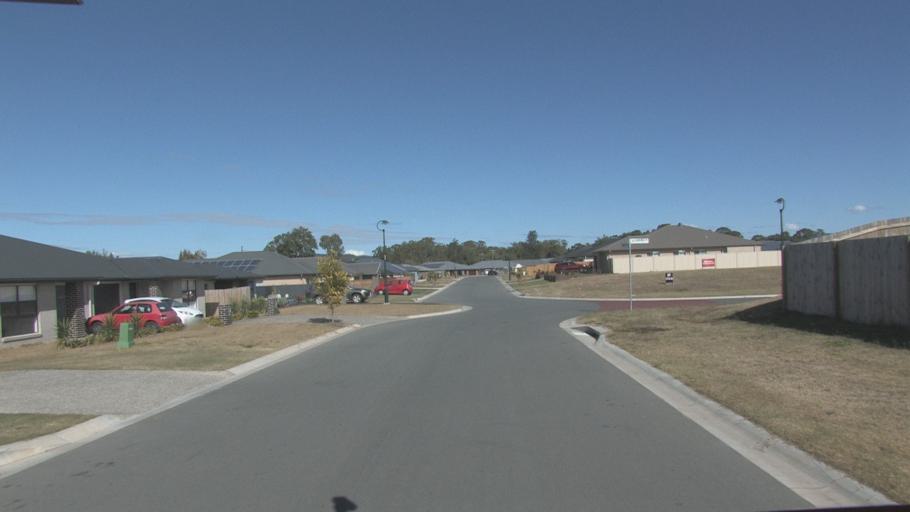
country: AU
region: Queensland
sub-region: Logan
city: Chambers Flat
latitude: -27.7766
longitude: 153.1016
